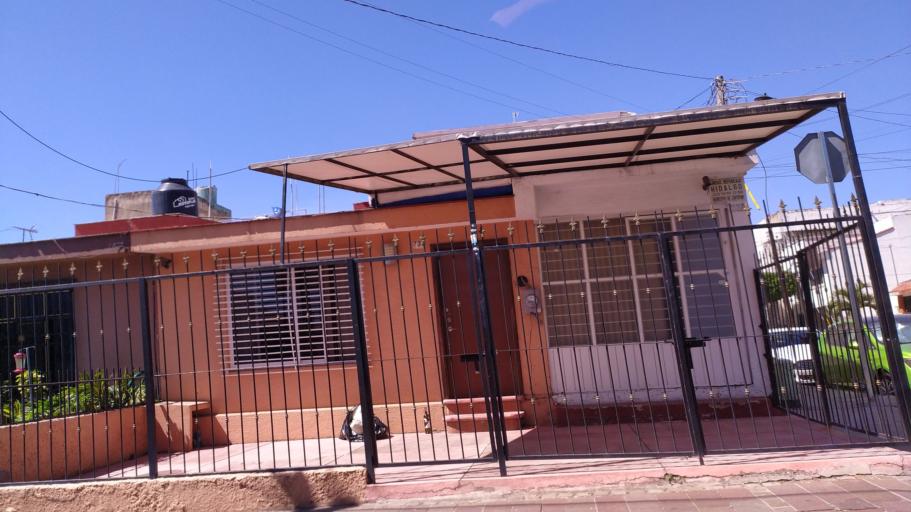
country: MX
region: Jalisco
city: Zapopan2
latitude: 20.7229
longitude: -103.3984
